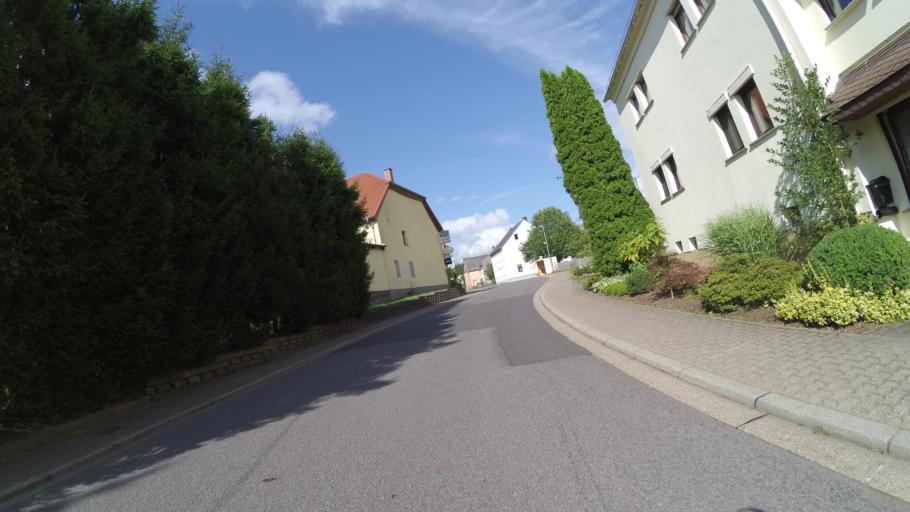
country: DE
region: Rheinland-Pfalz
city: Neuhutten
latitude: 49.5955
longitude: 7.0190
